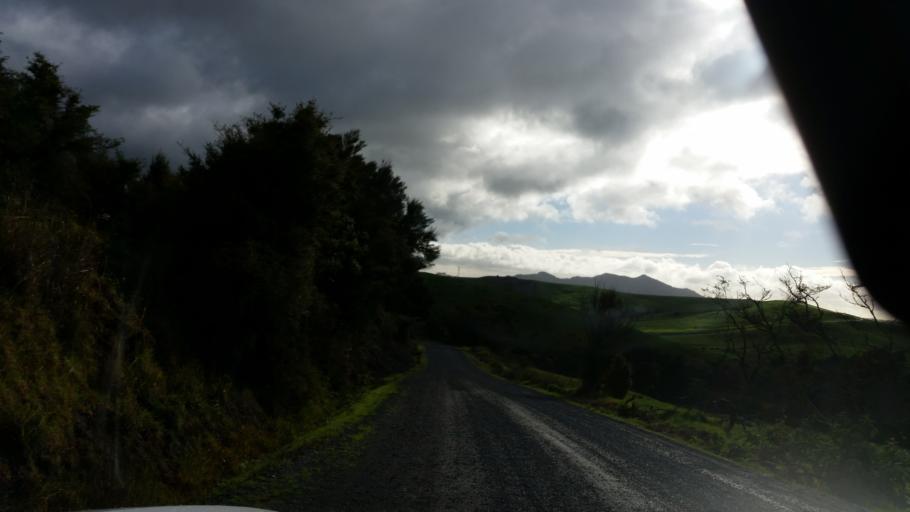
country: NZ
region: Northland
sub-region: Whangarei
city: Maungatapere
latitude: -35.6994
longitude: 174.1009
